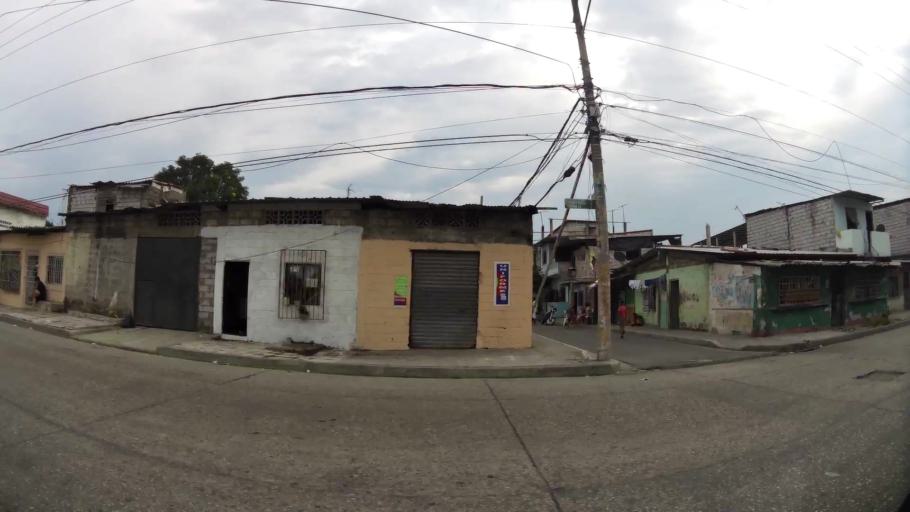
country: EC
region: Guayas
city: Guayaquil
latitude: -2.2454
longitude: -79.8825
